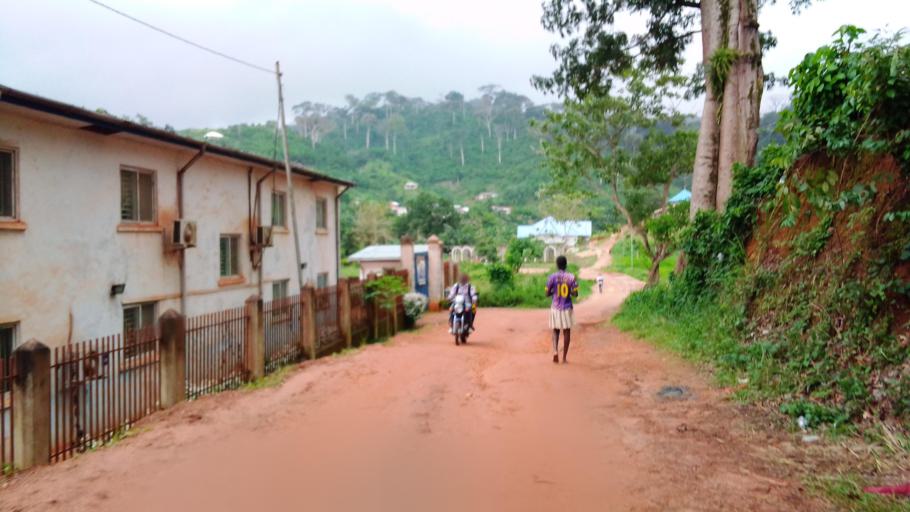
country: SL
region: Eastern Province
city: Kenema
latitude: 7.8797
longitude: -11.1975
